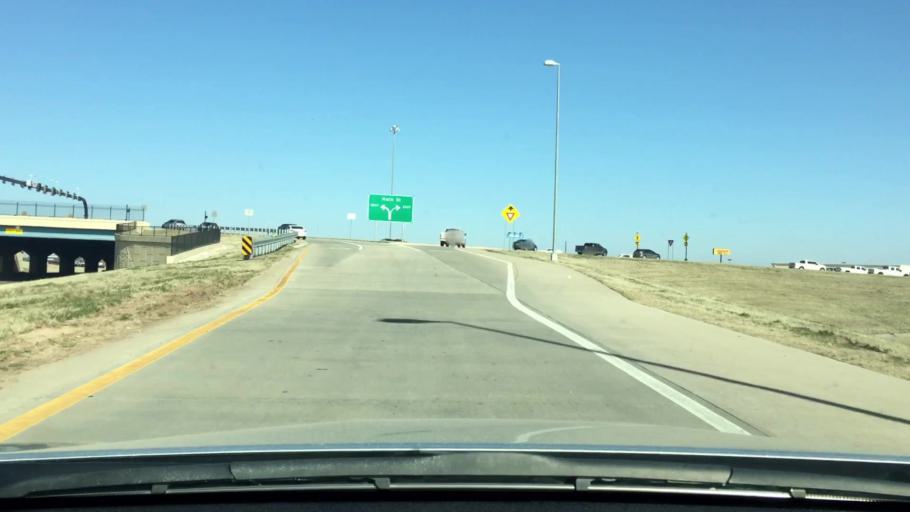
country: US
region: Oklahoma
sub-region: Cleveland County
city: Norman
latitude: 35.2170
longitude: -97.4848
